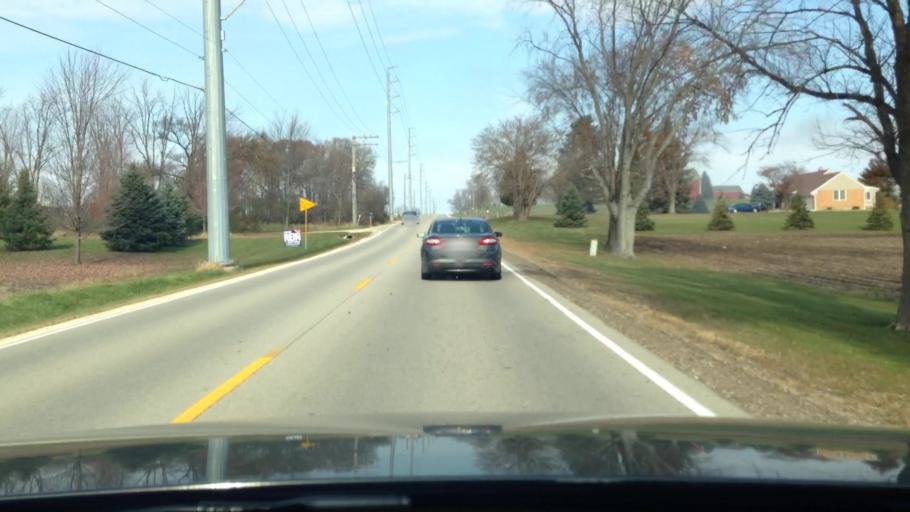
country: US
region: Illinois
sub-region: McHenry County
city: Woodstock
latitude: 42.2865
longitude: -88.4526
